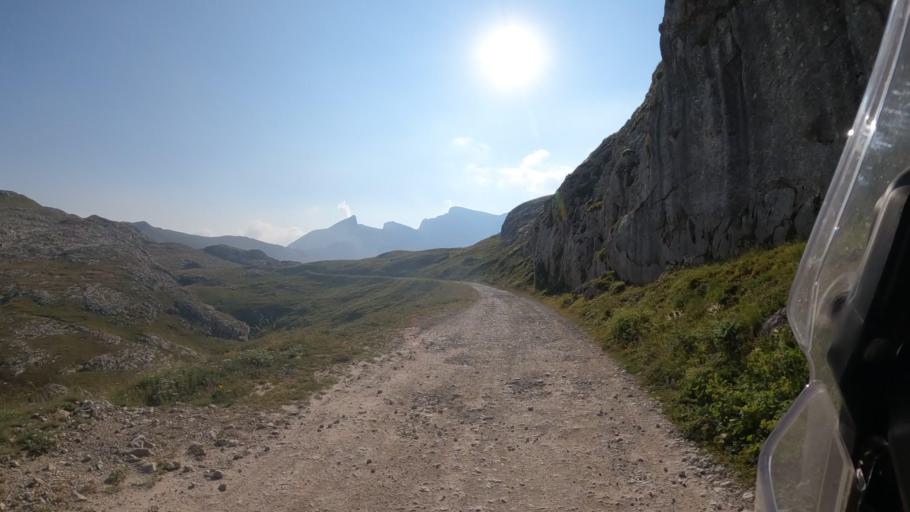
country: IT
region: Piedmont
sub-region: Provincia di Cuneo
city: Limone Piemonte
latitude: 44.1697
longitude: 7.6512
